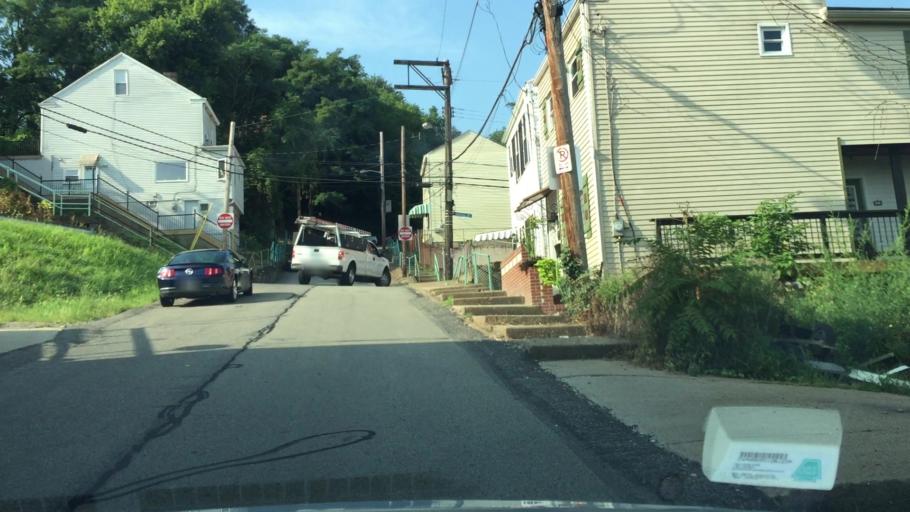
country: US
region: Pennsylvania
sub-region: Allegheny County
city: Mount Oliver
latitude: 40.4229
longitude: -79.9703
